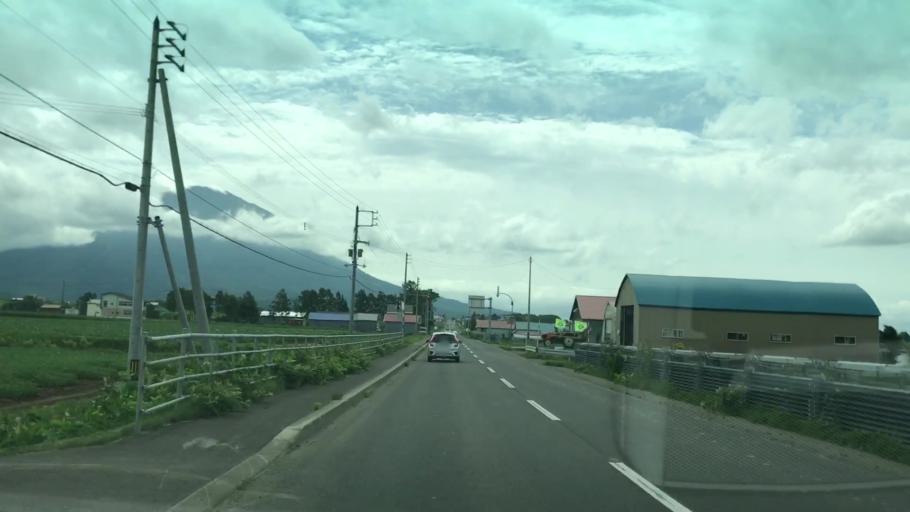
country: JP
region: Hokkaido
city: Niseko Town
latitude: 42.9318
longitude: 140.7759
